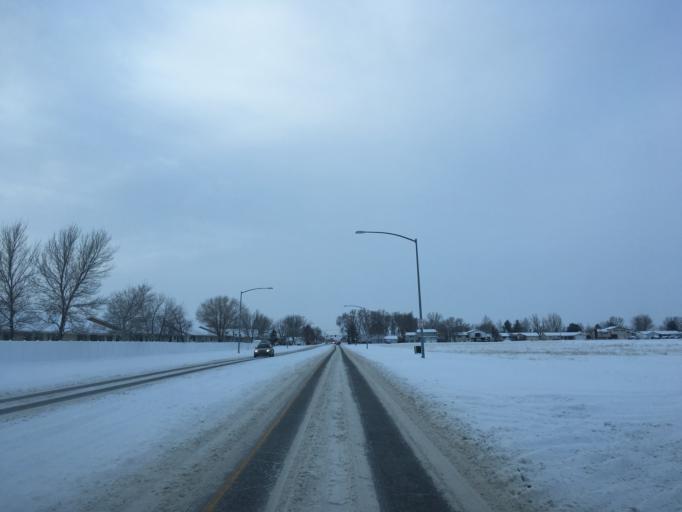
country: US
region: Montana
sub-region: Yellowstone County
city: Billings
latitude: 45.7742
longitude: -108.5970
